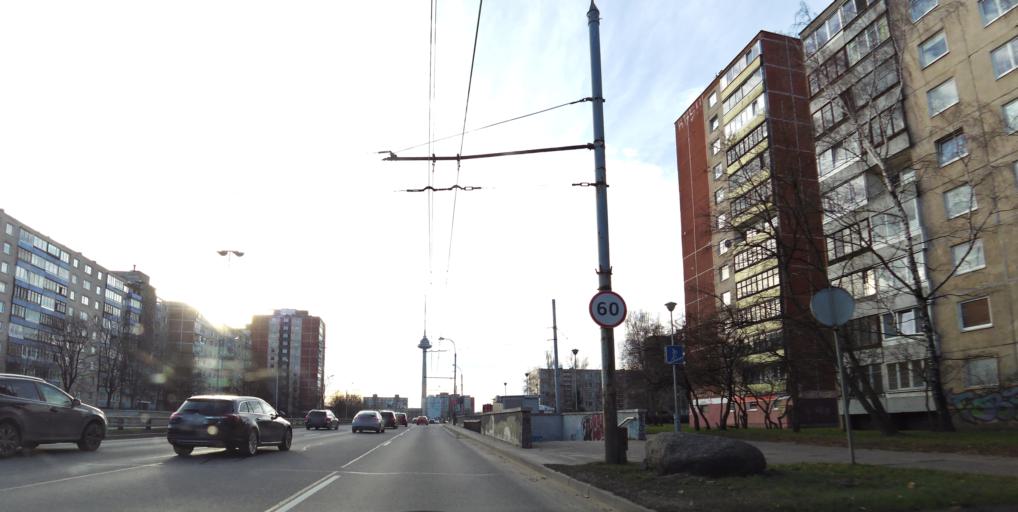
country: LT
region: Vilnius County
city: Justiniskes
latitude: 54.6975
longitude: 25.2206
